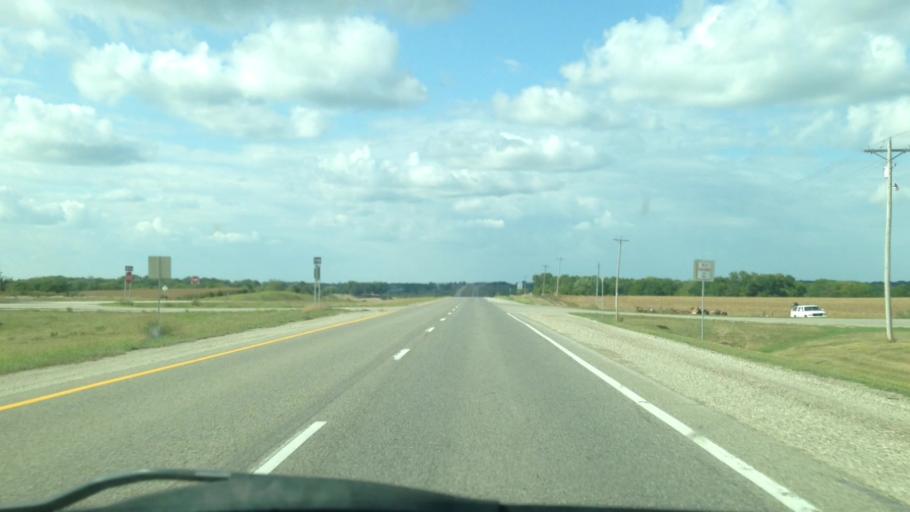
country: US
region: Iowa
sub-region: Henry County
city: Mount Pleasant
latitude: 40.8485
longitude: -91.5645
